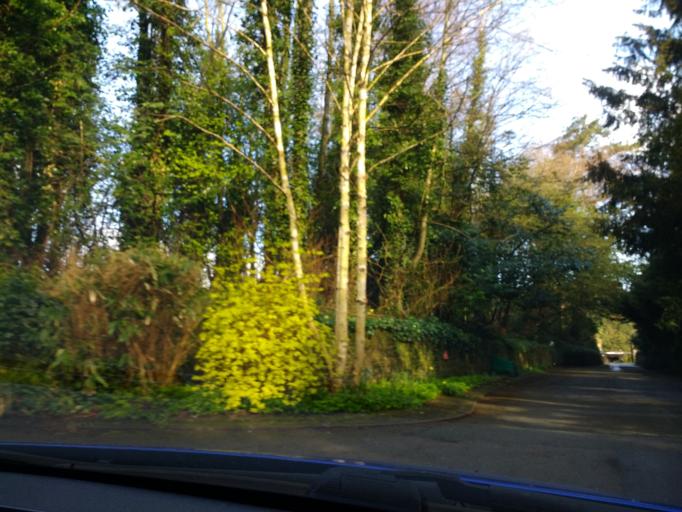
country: GB
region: England
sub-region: Lancashire
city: Caton
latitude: 54.0765
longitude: -2.7245
